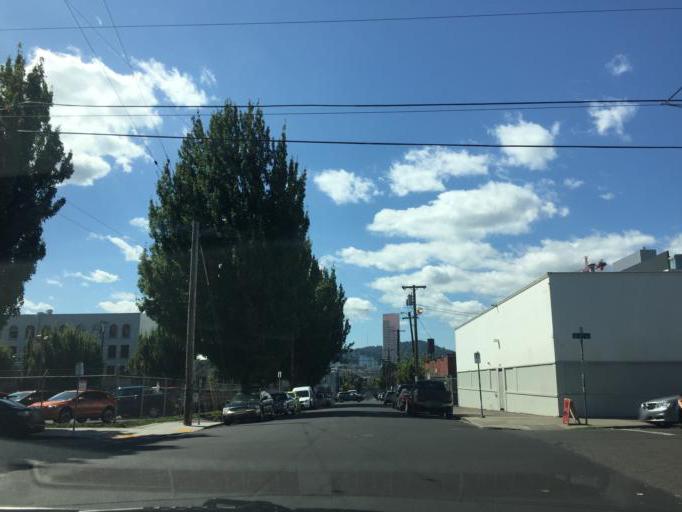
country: US
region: Oregon
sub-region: Multnomah County
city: Portland
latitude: 45.5223
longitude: -122.6584
